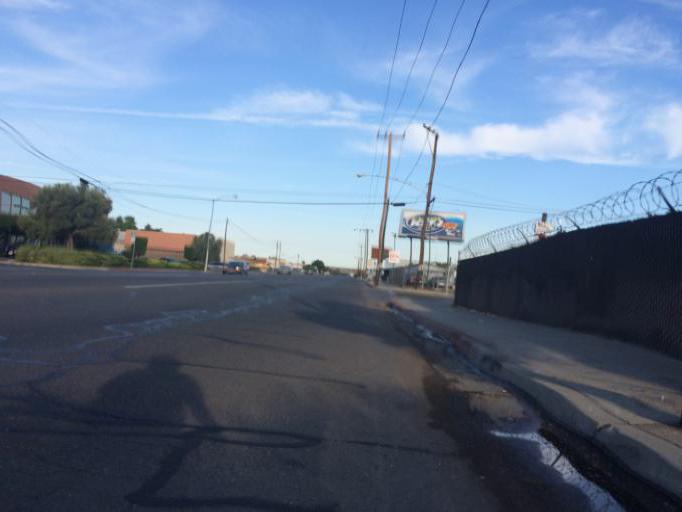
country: US
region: California
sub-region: Fresno County
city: Fresno
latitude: 36.7577
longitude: -119.7404
